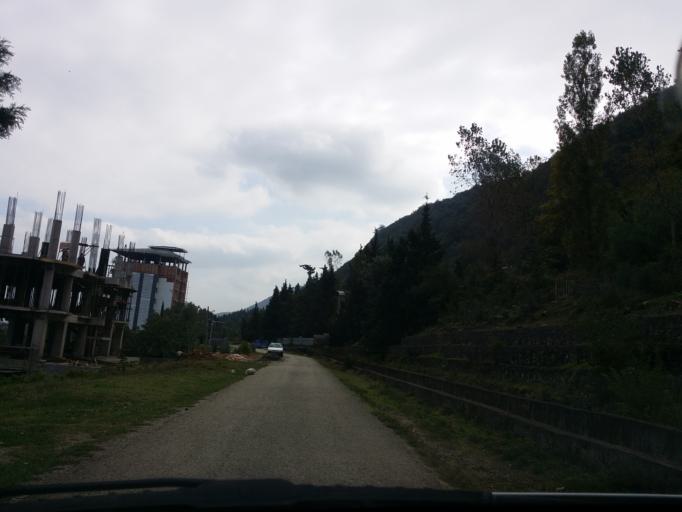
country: IR
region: Mazandaran
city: Chalus
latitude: 36.6525
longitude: 51.3497
